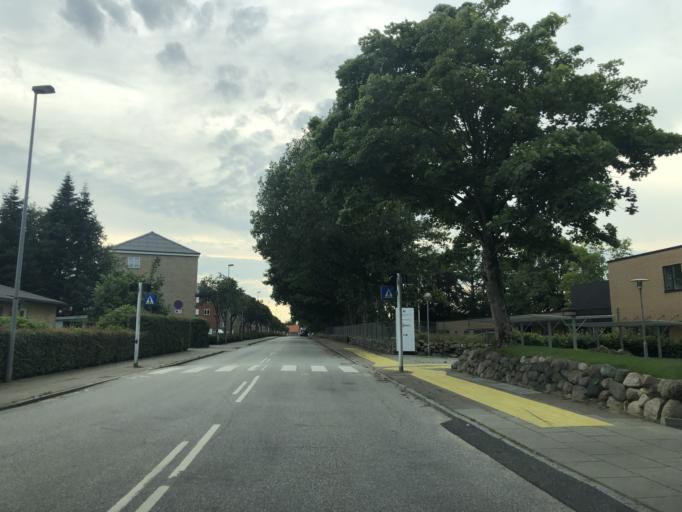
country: DK
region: Central Jutland
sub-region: Herning Kommune
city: Herning
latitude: 56.1432
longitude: 8.9659
